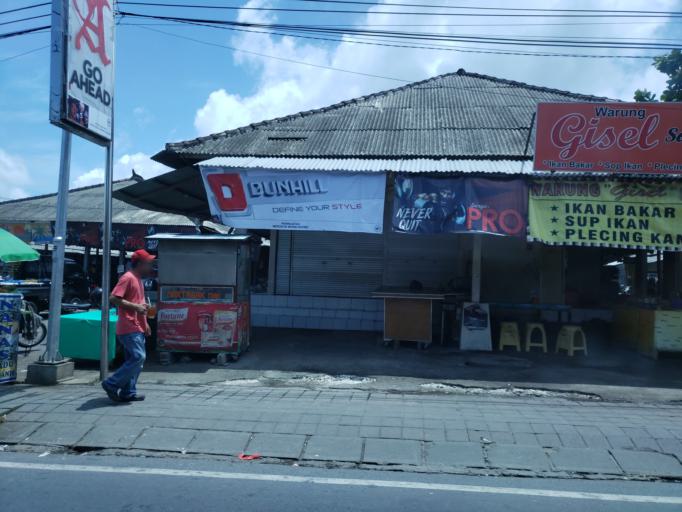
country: ID
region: Bali
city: Jimbaran
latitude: -8.8030
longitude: 115.1599
